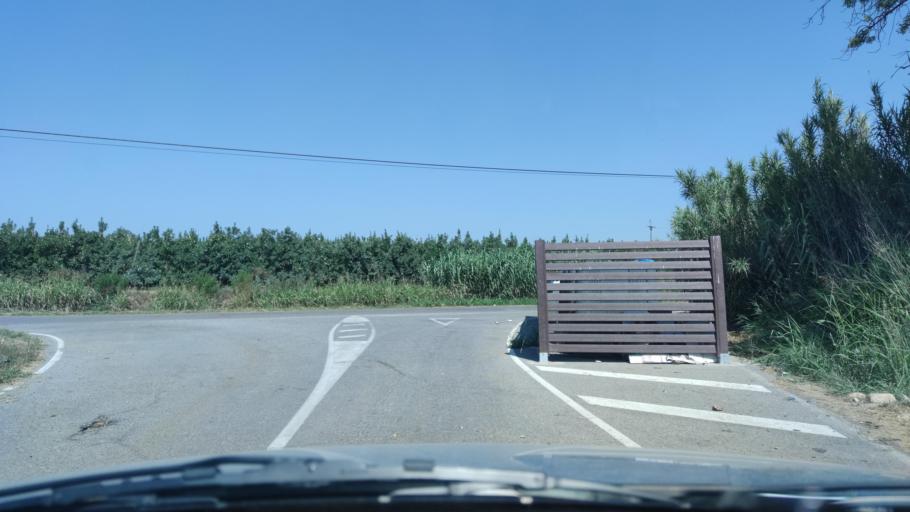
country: ES
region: Catalonia
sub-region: Provincia de Lleida
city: Torrefarrera
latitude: 41.6423
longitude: 0.5875
